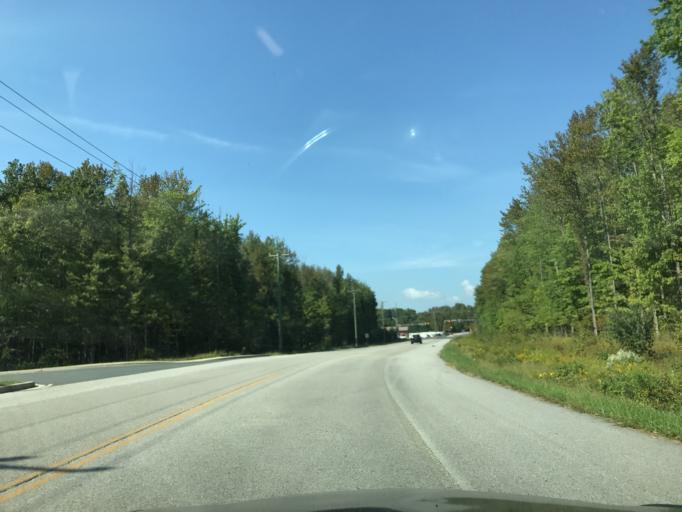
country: US
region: Maryland
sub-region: Cecil County
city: Perryville
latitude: 39.5692
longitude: -76.0653
